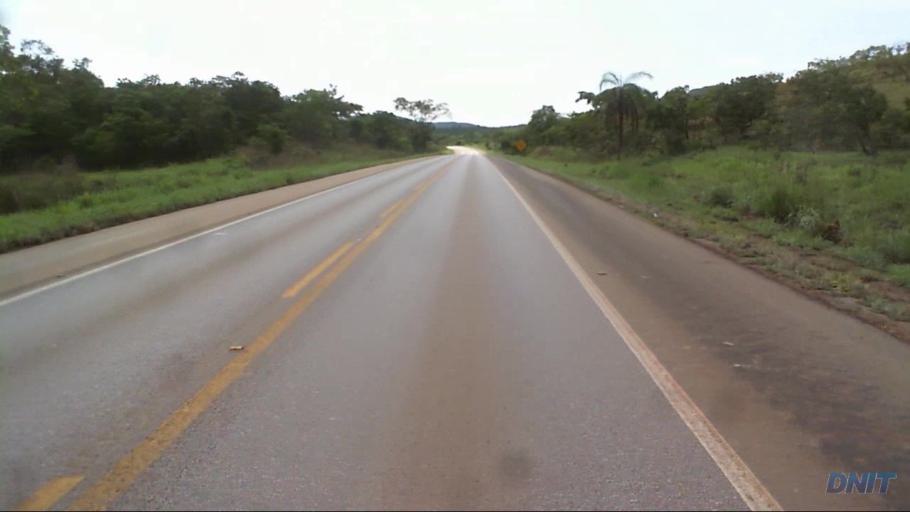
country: BR
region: Goias
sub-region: Barro Alto
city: Barro Alto
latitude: -15.1426
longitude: -48.8205
